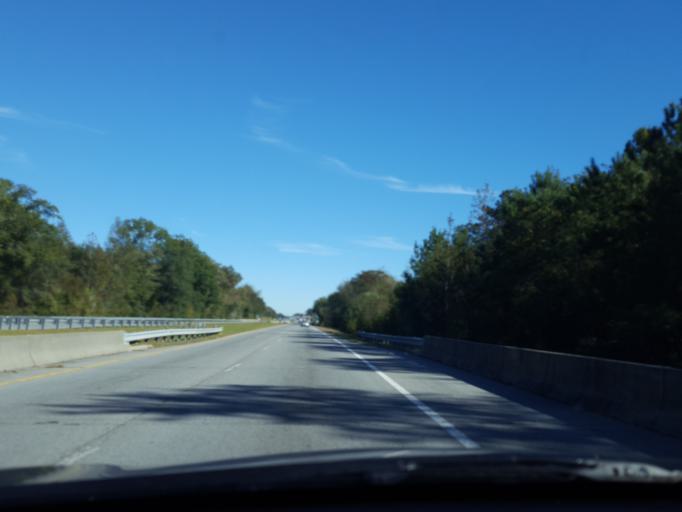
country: US
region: North Carolina
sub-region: Beaufort County
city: Washington
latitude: 35.6059
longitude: -77.1449
